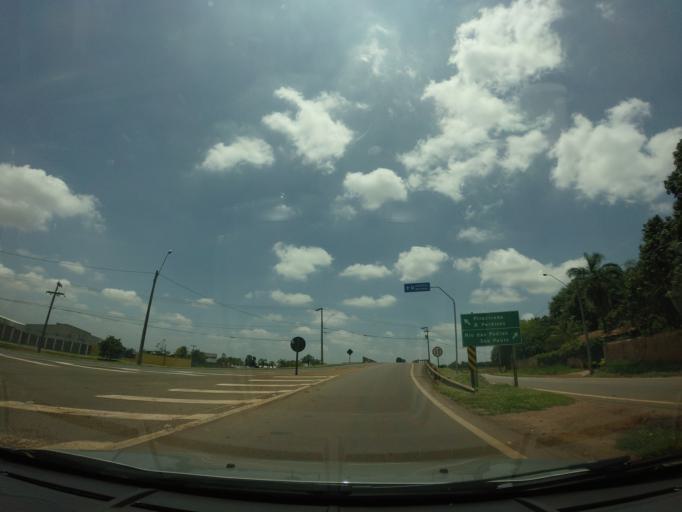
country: BR
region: Sao Paulo
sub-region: Piracicaba
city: Piracicaba
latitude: -22.7638
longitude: -47.5964
